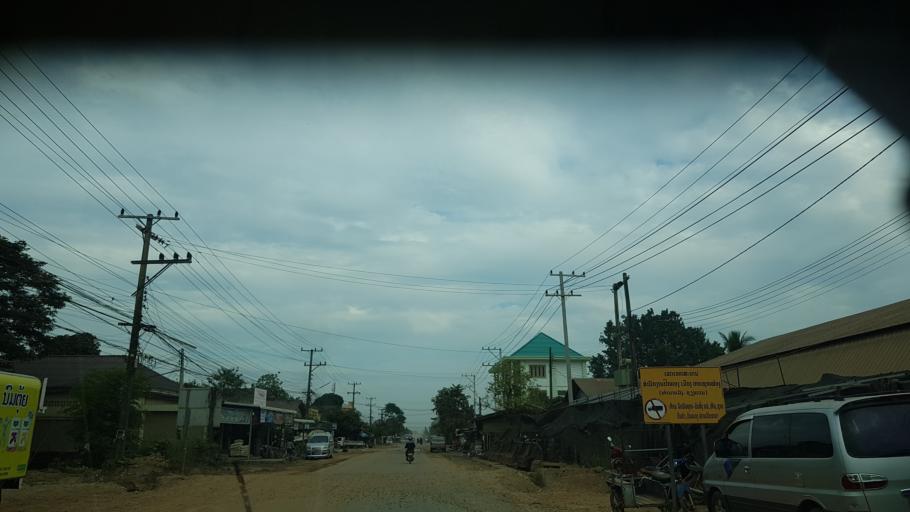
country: TH
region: Nong Khai
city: Nong Khai
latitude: 17.8861
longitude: 102.7213
